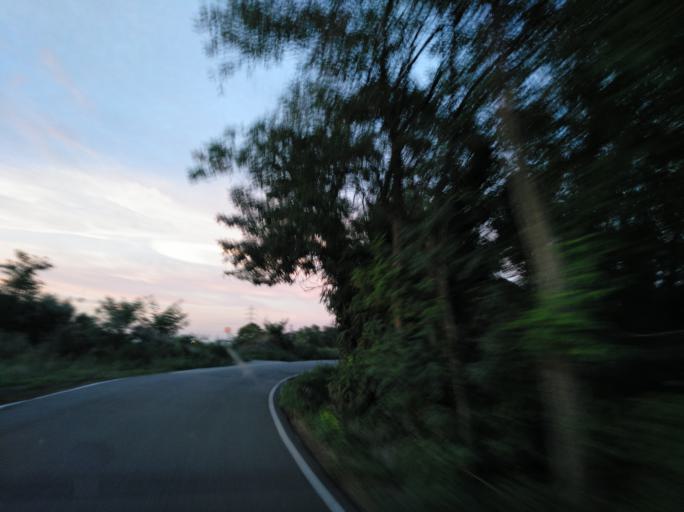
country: ES
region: Catalonia
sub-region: Provincia de Girona
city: Salt
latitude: 41.9593
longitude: 2.7949
